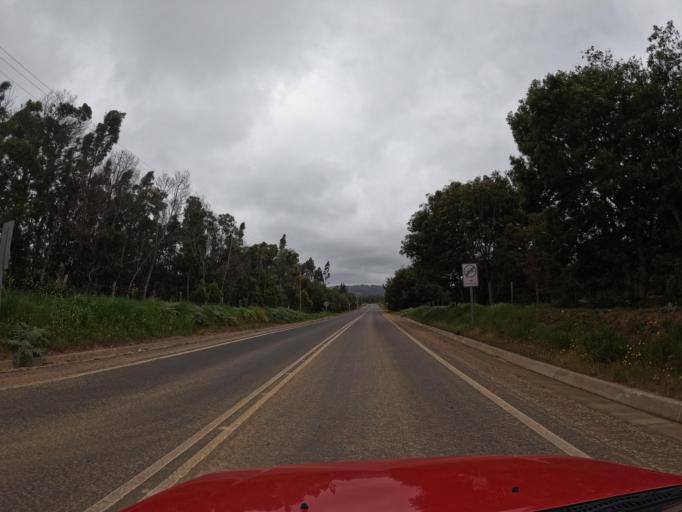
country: CL
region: O'Higgins
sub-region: Provincia de Colchagua
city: Santa Cruz
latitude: -34.5094
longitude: -72.0047
